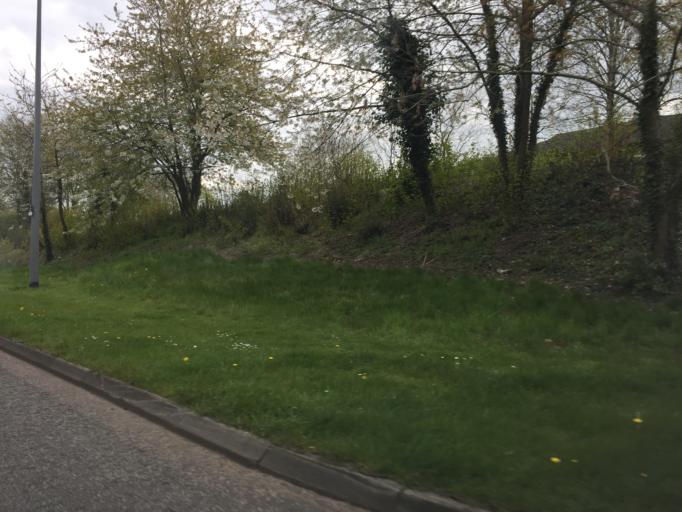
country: GB
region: England
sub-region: Milton Keynes
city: Milton Keynes
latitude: 52.0463
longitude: -0.7650
